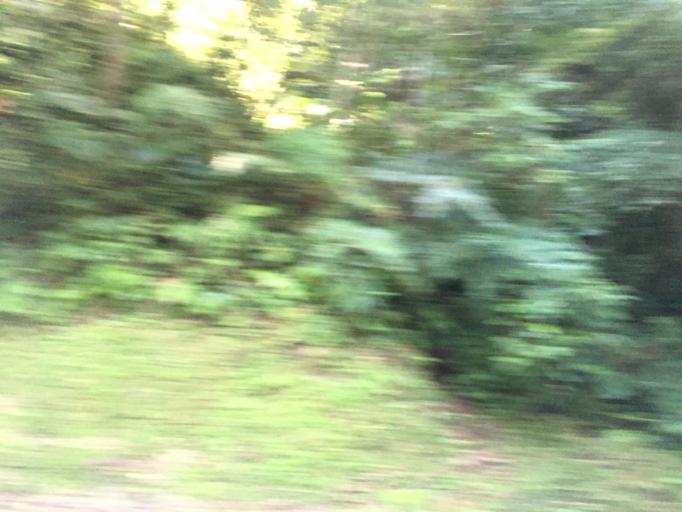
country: TW
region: Taiwan
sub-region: Yilan
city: Yilan
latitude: 24.7574
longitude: 121.6196
